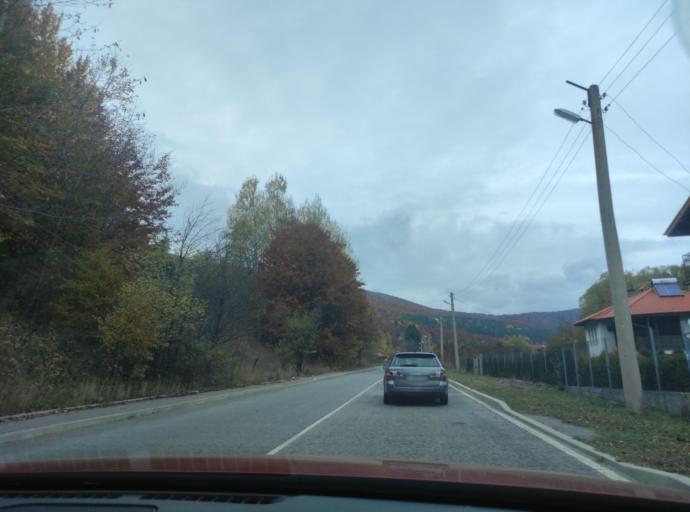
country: BG
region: Sofiya
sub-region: Obshtina Godech
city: Godech
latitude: 43.0865
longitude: 23.1013
